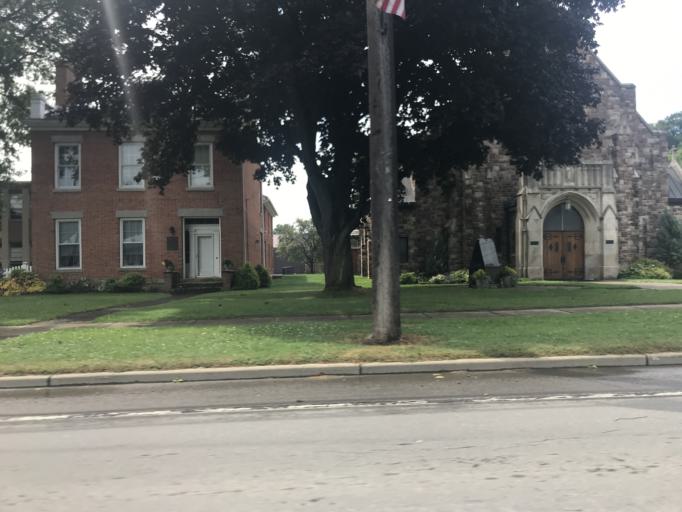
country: US
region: New York
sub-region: Chautauqua County
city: Silver Creek
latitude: 42.5451
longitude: -79.1706
